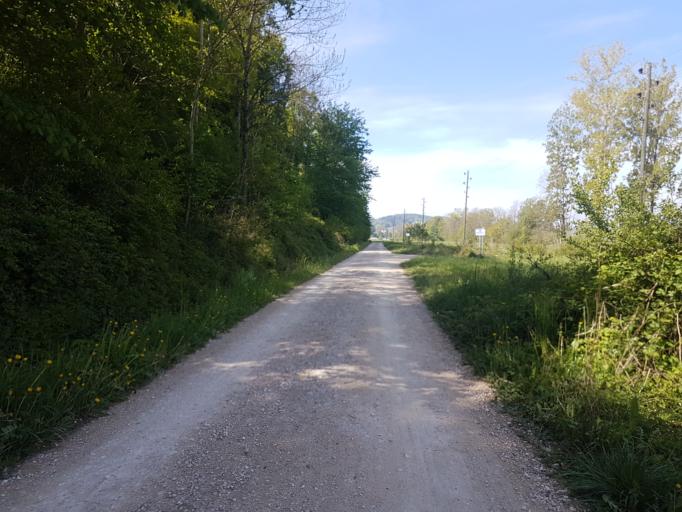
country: CH
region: Bern
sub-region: Seeland District
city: Tauffelen
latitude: 47.0537
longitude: 7.1713
